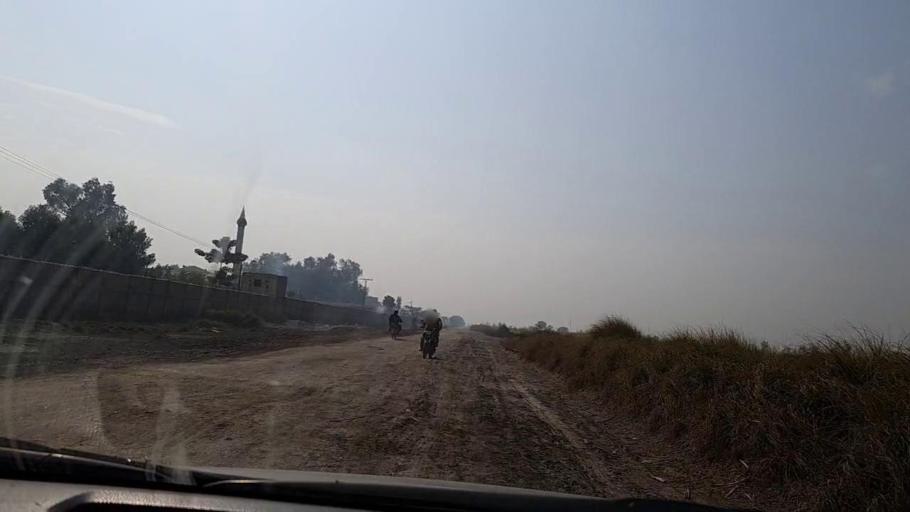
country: PK
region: Sindh
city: Daulatpur
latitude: 26.5558
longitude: 67.9832
